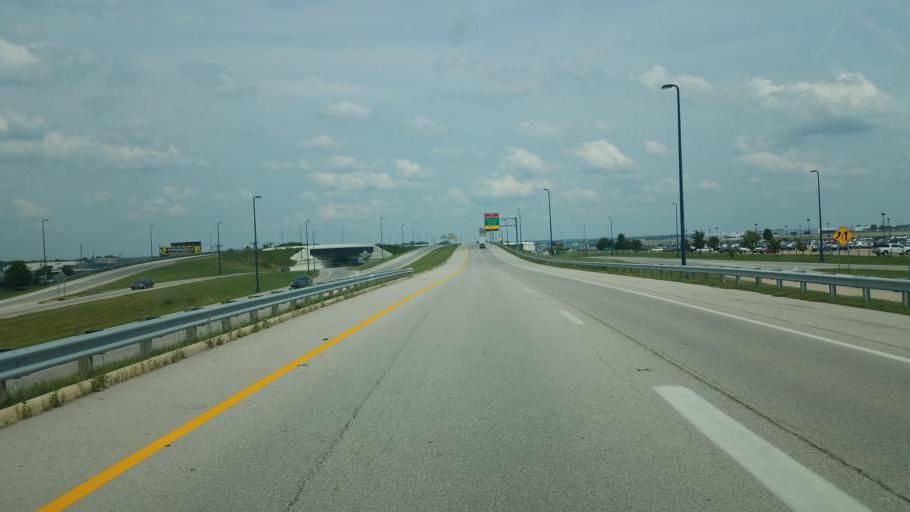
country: US
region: Ohio
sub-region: Franklin County
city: Bexley
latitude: 39.9998
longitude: -82.9181
